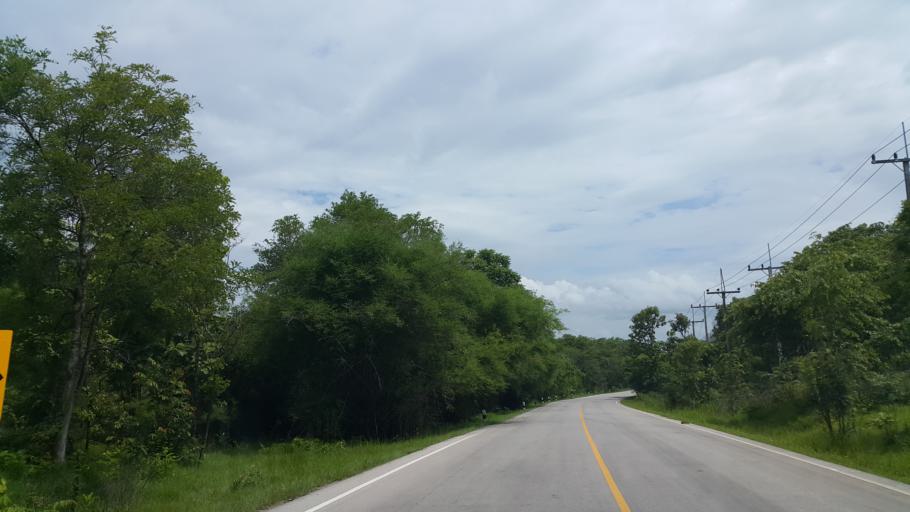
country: TH
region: Lampang
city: Mueang Pan
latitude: 18.7686
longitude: 99.5554
